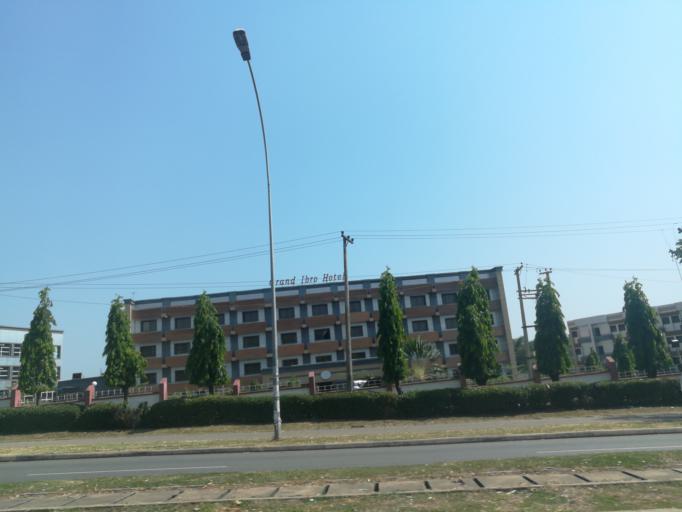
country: NG
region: Abuja Federal Capital Territory
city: Abuja
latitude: 9.0605
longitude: 7.4569
